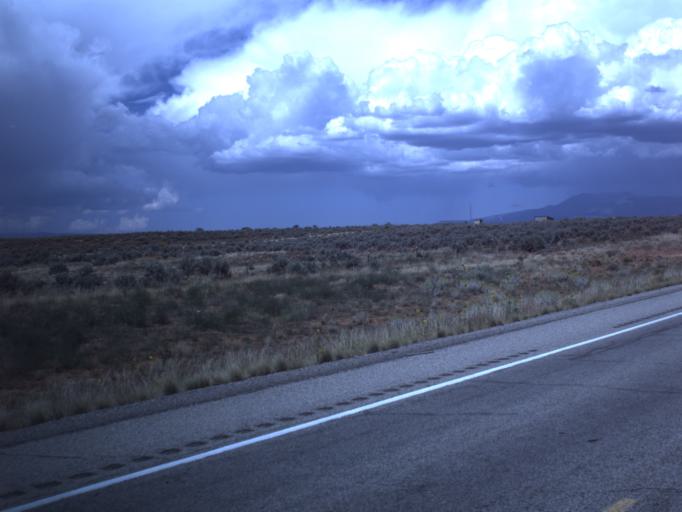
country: US
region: Utah
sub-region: San Juan County
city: Blanding
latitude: 37.5487
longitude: -109.4911
